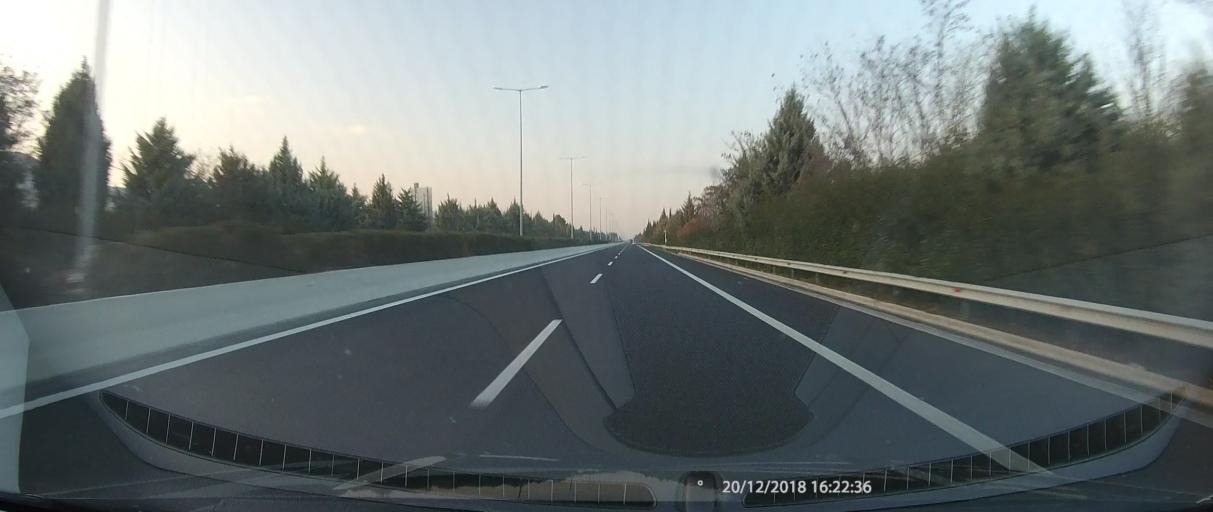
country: GR
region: Thessaly
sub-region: Nomos Magnisias
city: Sourpi
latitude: 39.0731
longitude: 22.8845
